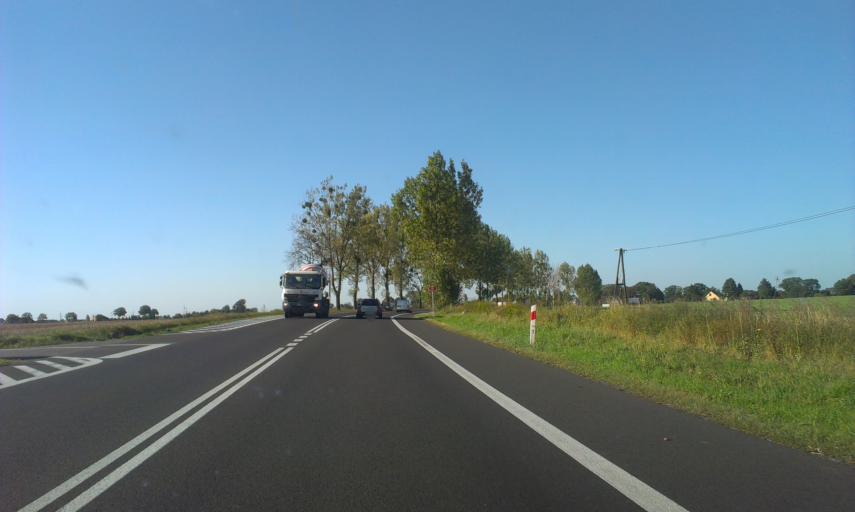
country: PL
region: Kujawsko-Pomorskie
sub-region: Powiat chelminski
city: Chelmno
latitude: 53.3101
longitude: 18.5090
